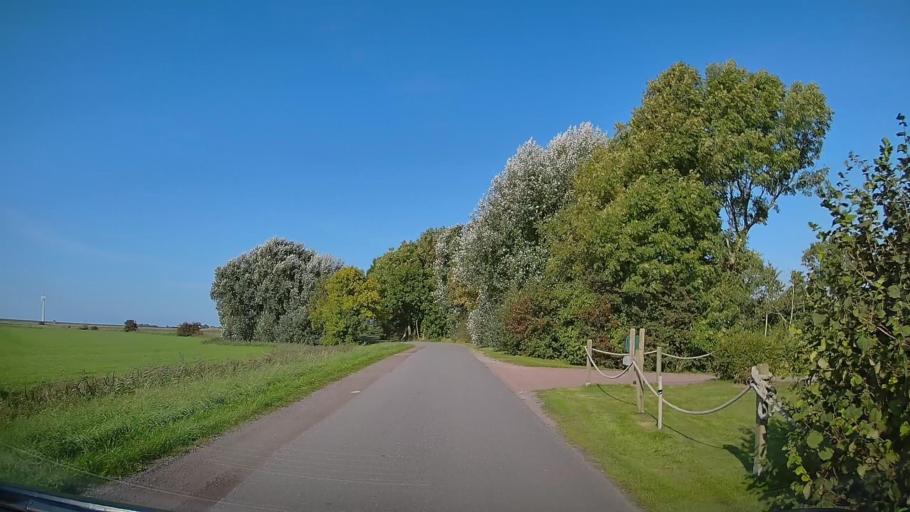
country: DE
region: Lower Saxony
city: Padingbuttel
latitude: 53.7186
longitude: 8.5191
